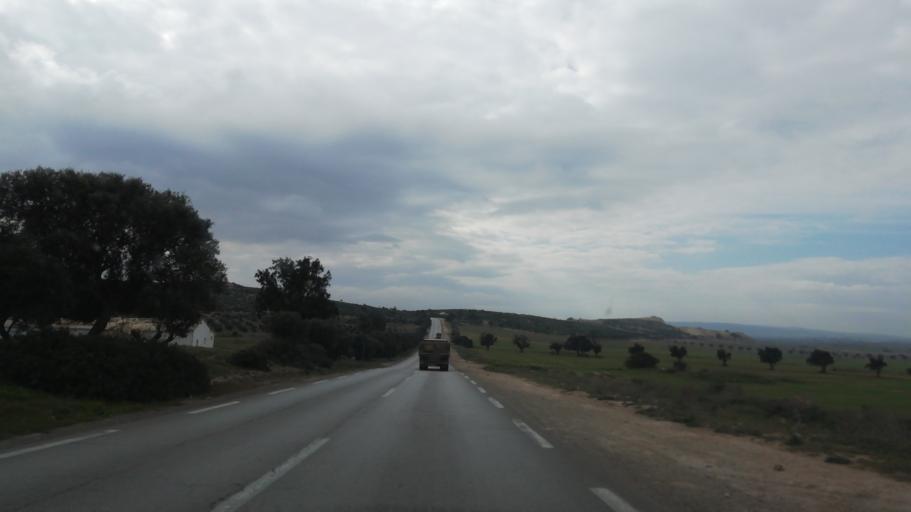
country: DZ
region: Oran
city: Ain el Bya
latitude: 35.7253
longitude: -0.3558
